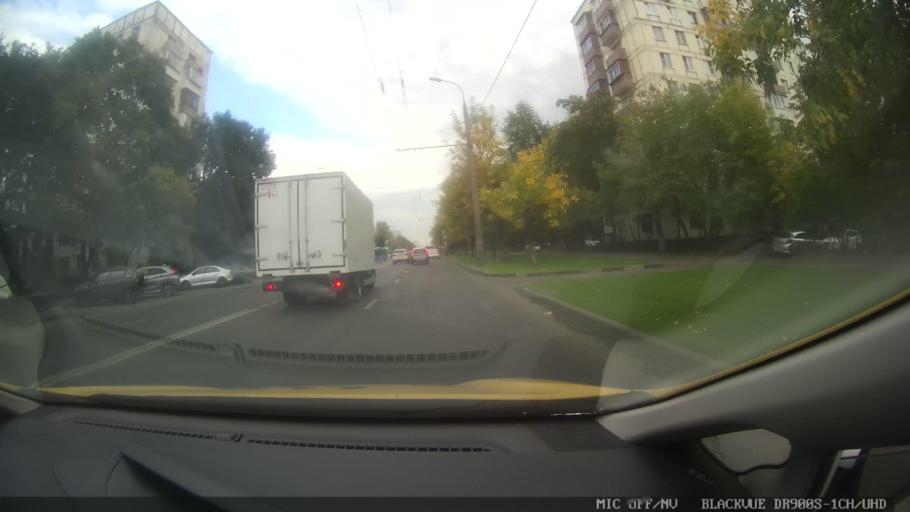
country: RU
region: Moscow
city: Novokuz'minki
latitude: 55.6992
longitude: 37.7725
